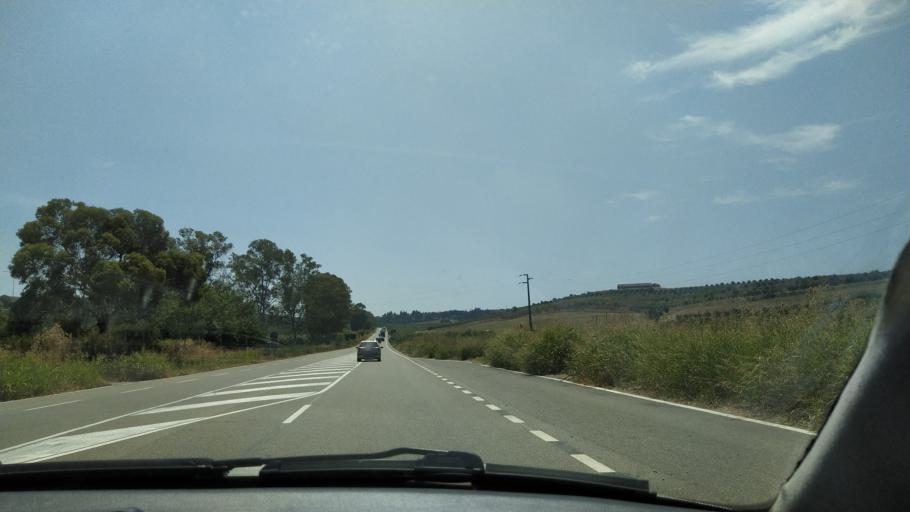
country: IT
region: Basilicate
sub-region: Provincia di Matera
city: Bernalda
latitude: 40.4438
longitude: 16.7808
